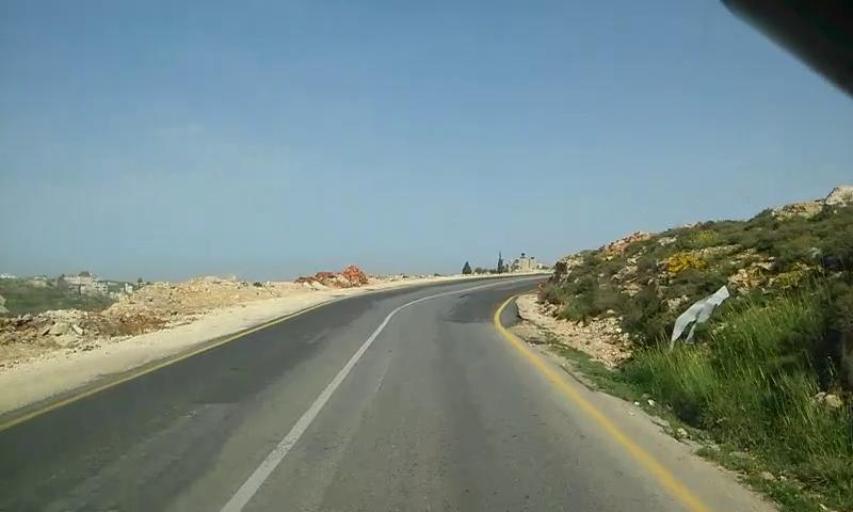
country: PS
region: West Bank
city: Surda
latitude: 31.9397
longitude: 35.2132
